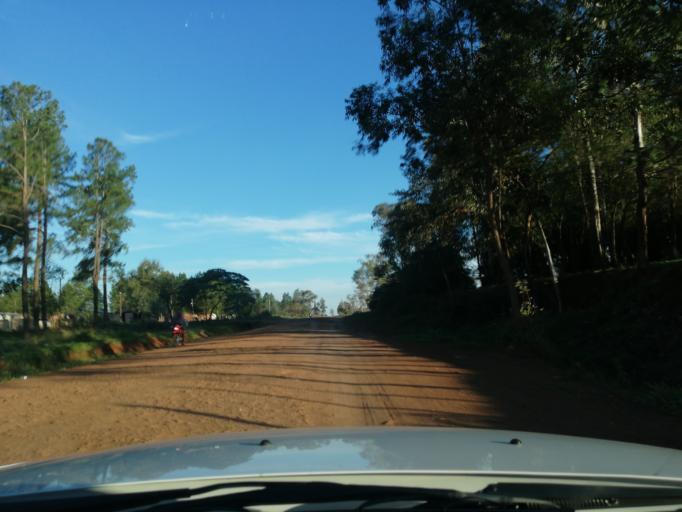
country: AR
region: Misiones
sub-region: Departamento de Capital
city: Posadas
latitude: -27.4768
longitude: -55.9709
